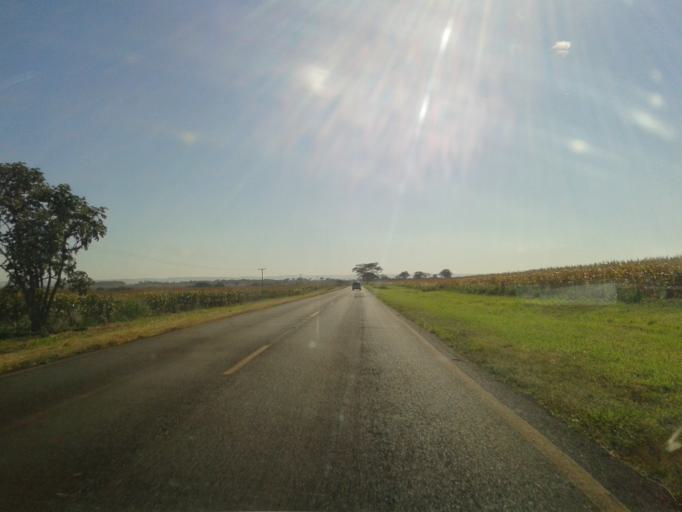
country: BR
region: Minas Gerais
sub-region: Capinopolis
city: Capinopolis
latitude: -18.6176
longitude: -49.5319
